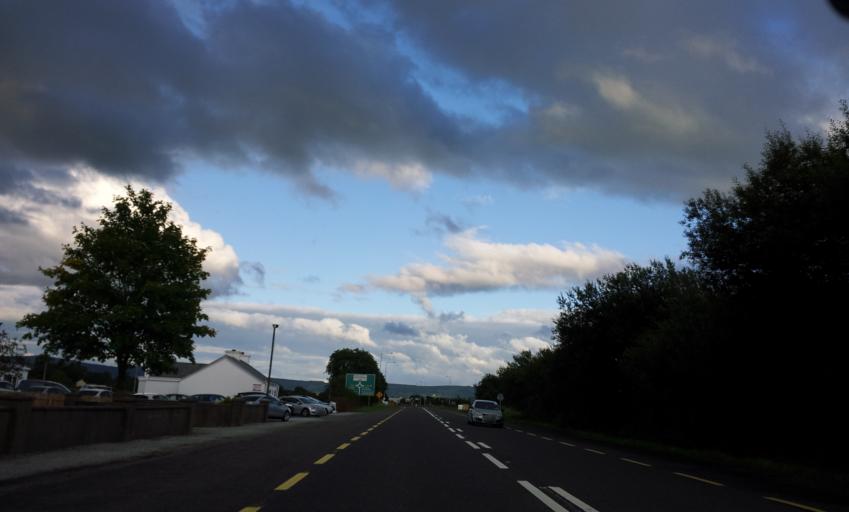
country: IE
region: Munster
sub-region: Ciarrai
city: Castleisland
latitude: 52.2371
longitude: -9.4900
